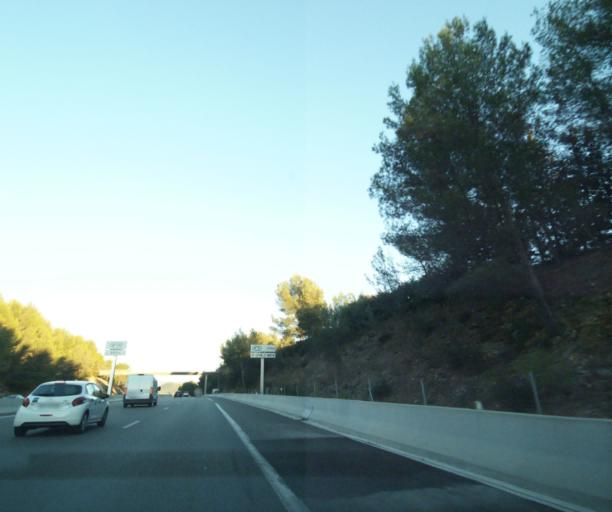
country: FR
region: Provence-Alpes-Cote d'Azur
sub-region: Departement du Var
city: Saint-Cyr-sur-Mer
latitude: 43.1926
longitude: 5.6787
